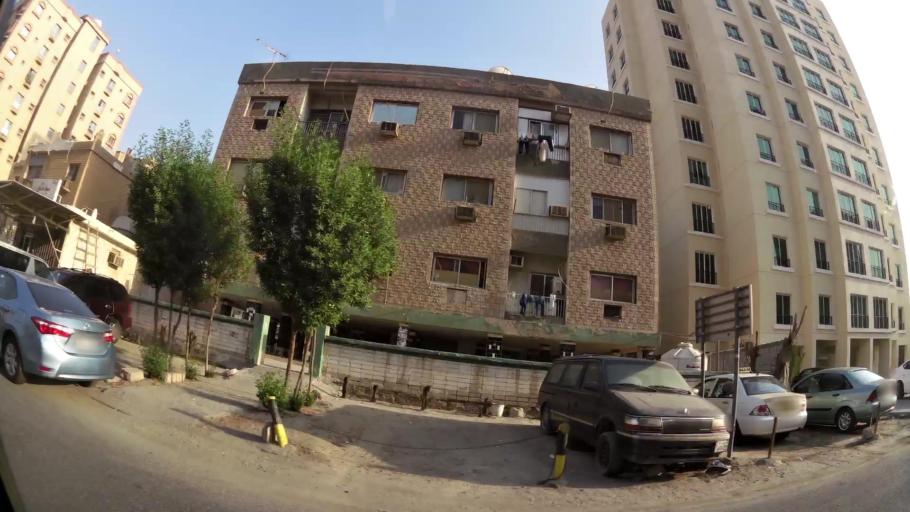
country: KW
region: Muhafazat Hawalli
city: As Salimiyah
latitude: 29.3298
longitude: 48.0525
